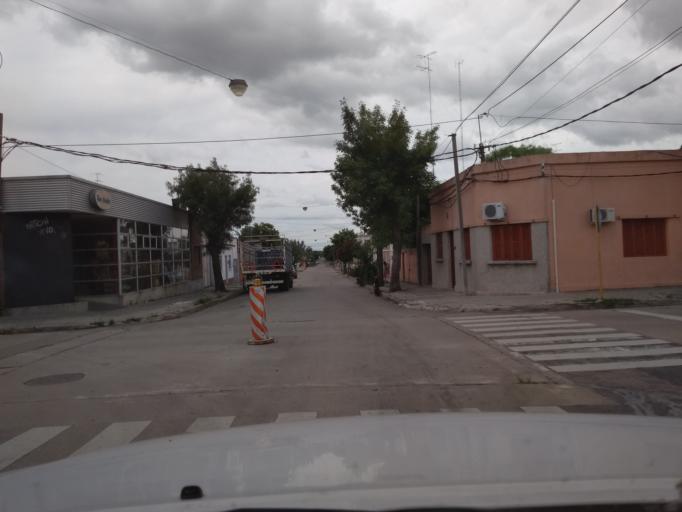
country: UY
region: Florida
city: Florida
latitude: -34.0978
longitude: -56.2119
